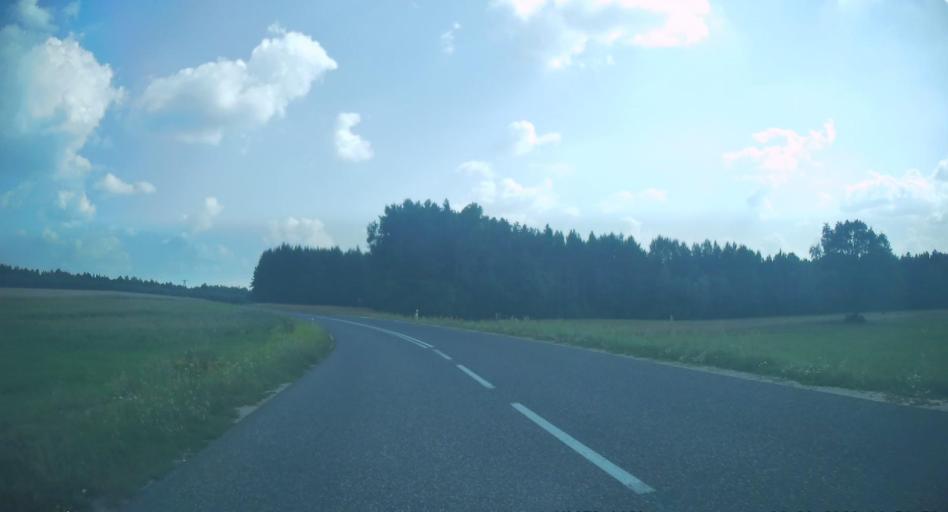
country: PL
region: Swietokrzyskie
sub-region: Powiat kielecki
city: Lopuszno
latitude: 50.9016
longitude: 20.2475
